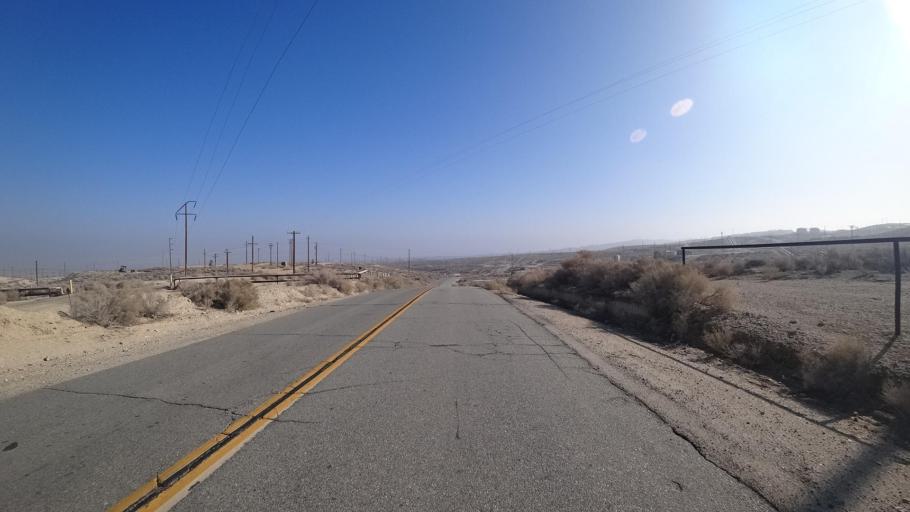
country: US
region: California
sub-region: Kern County
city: Taft Heights
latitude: 35.1441
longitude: -119.5108
